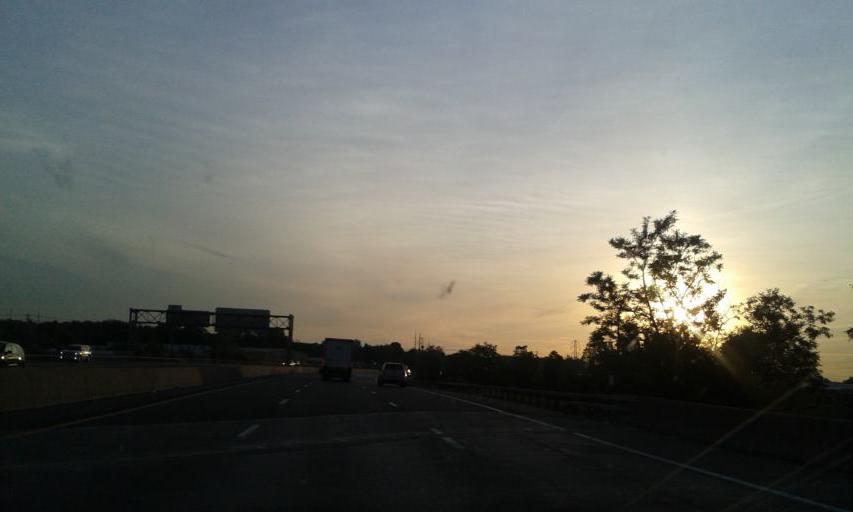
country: US
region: New York
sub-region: Onondaga County
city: Lakeland
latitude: 43.1067
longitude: -76.2508
